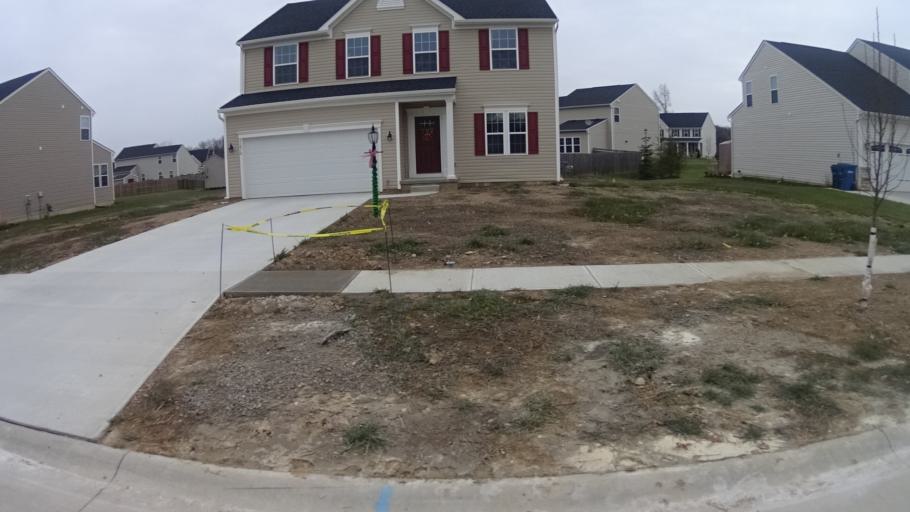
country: US
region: Ohio
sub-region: Lorain County
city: North Ridgeville
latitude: 41.3674
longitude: -81.9727
